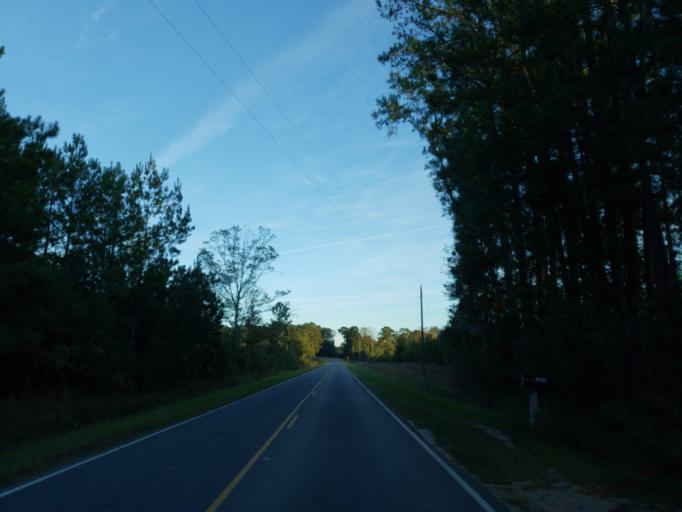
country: US
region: Mississippi
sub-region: Wayne County
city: Belmont
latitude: 31.4434
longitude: -88.5126
